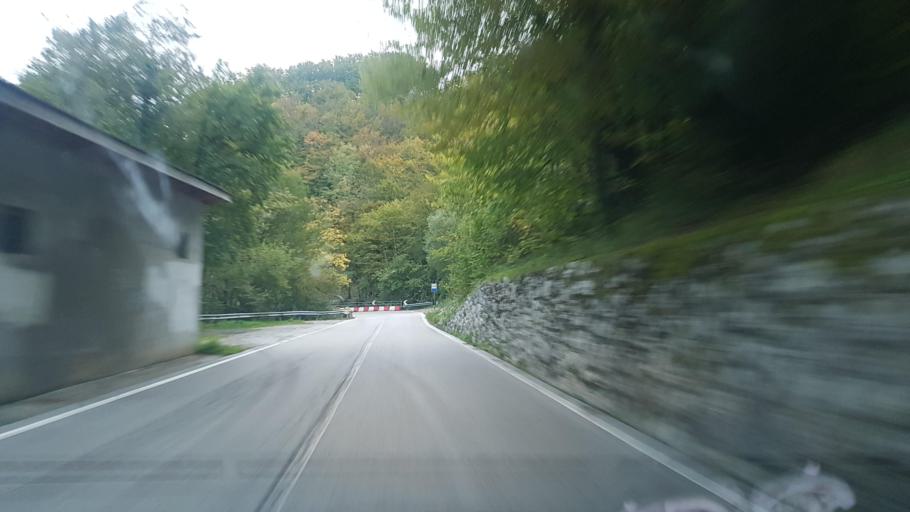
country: IT
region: Friuli Venezia Giulia
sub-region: Provincia di Pordenone
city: Anduins
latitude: 46.2720
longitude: 12.9446
